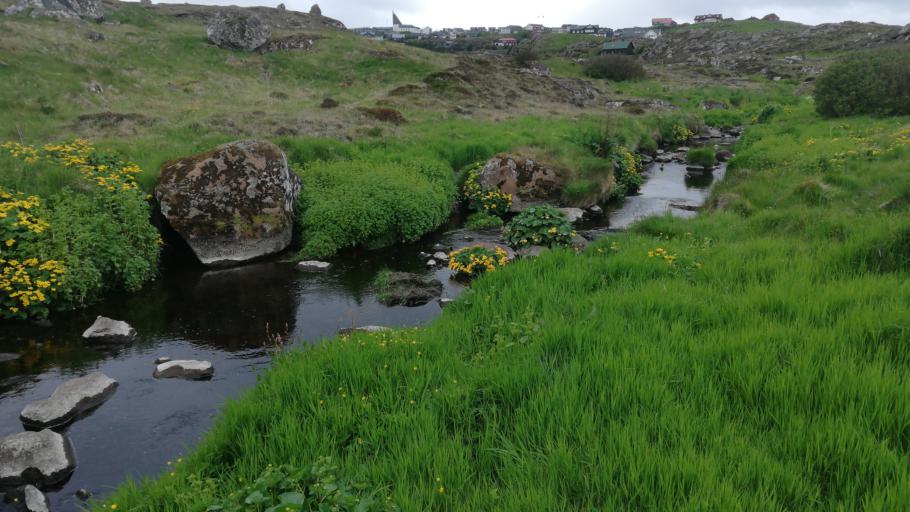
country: FO
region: Streymoy
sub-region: Torshavn
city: Torshavn
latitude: 62.0237
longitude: -6.7588
